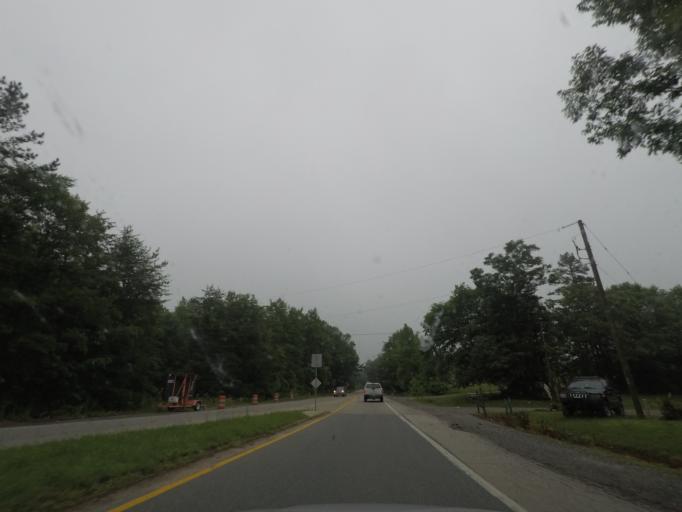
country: US
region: Virginia
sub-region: Prince Edward County
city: Farmville
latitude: 37.3186
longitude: -78.4612
